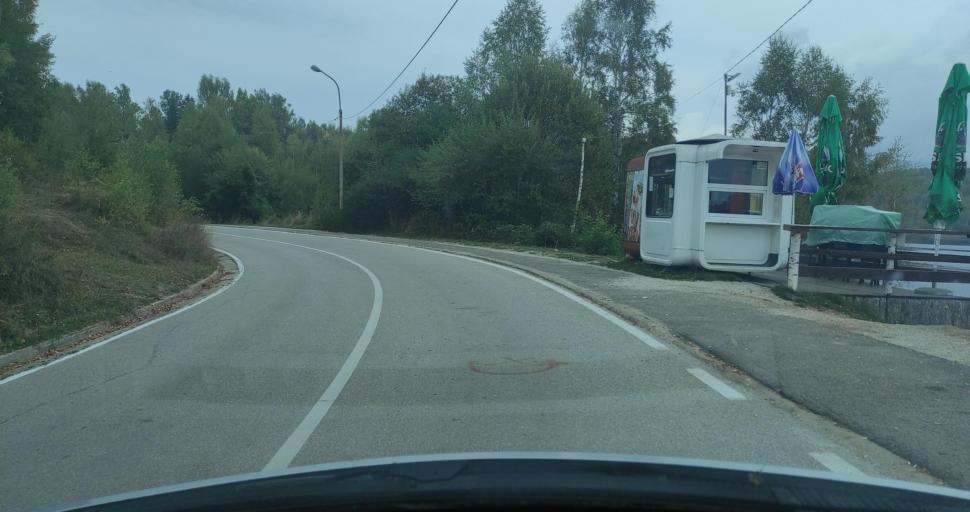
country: RS
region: Central Serbia
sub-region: Jablanicki Okrug
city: Crna Trava
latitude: 42.7393
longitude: 22.3298
